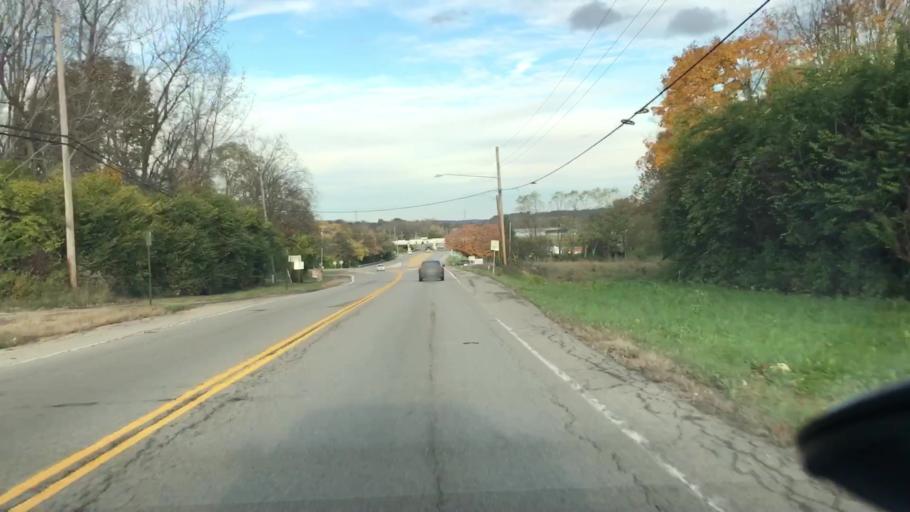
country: US
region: Ohio
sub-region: Greene County
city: Fairborn
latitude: 39.8428
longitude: -83.9989
